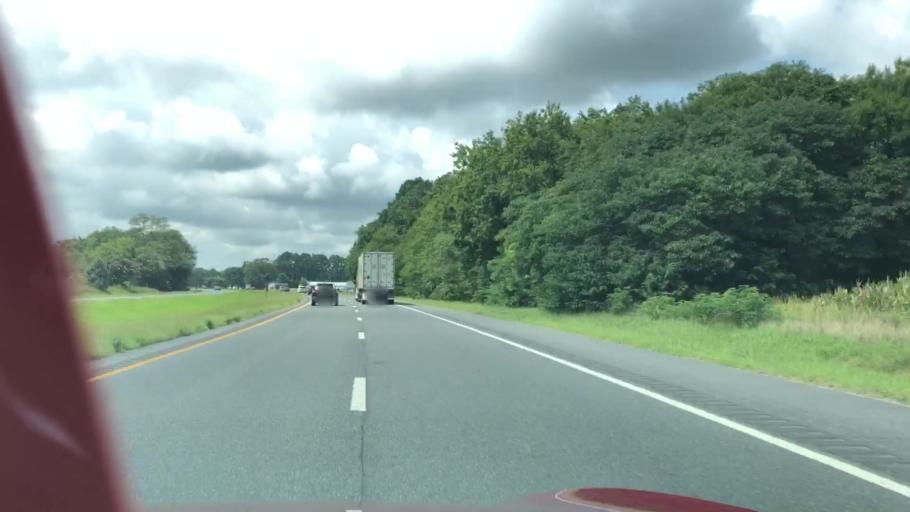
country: US
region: Virginia
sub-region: Northampton County
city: Eastville
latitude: 37.4013
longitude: -75.9088
